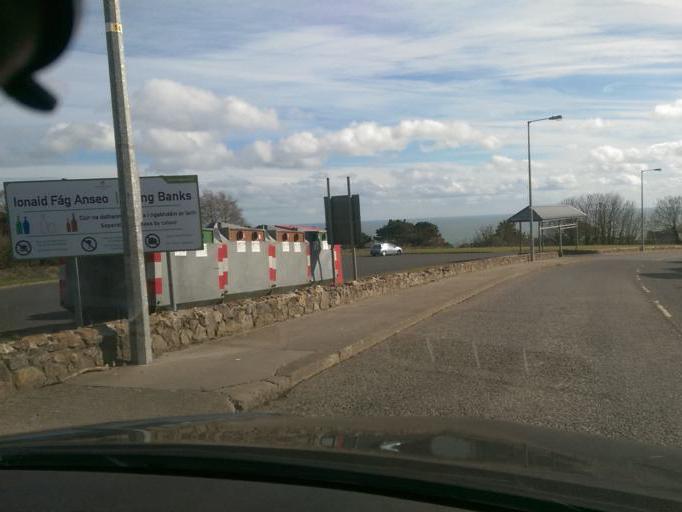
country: IE
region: Leinster
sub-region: Fingal County
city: Howth
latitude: 53.3695
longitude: -6.0606
